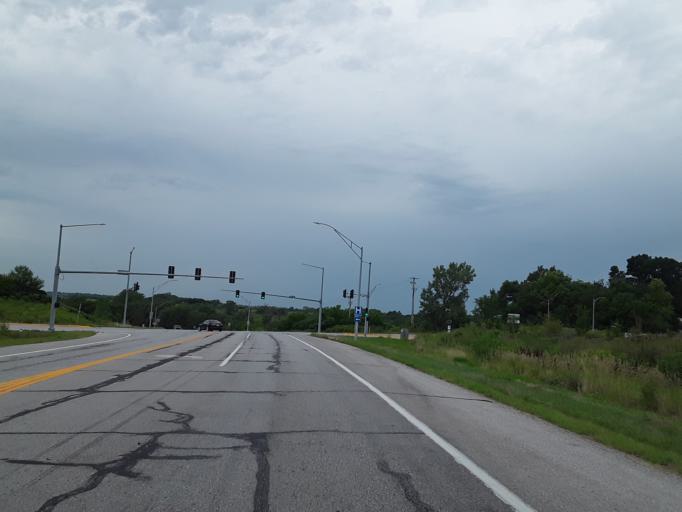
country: US
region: Iowa
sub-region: Pottawattamie County
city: Carter Lake
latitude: 41.3638
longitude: -96.0225
